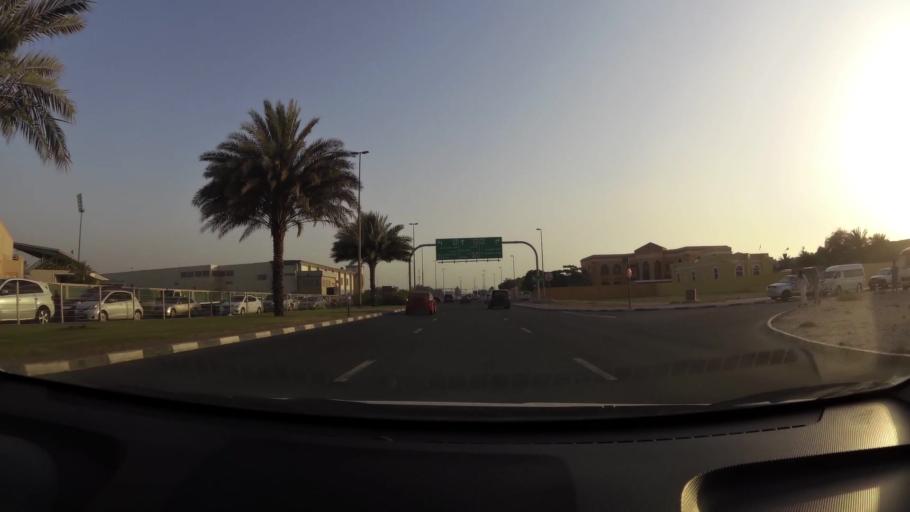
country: AE
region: Ash Shariqah
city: Sharjah
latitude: 25.2922
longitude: 55.3473
